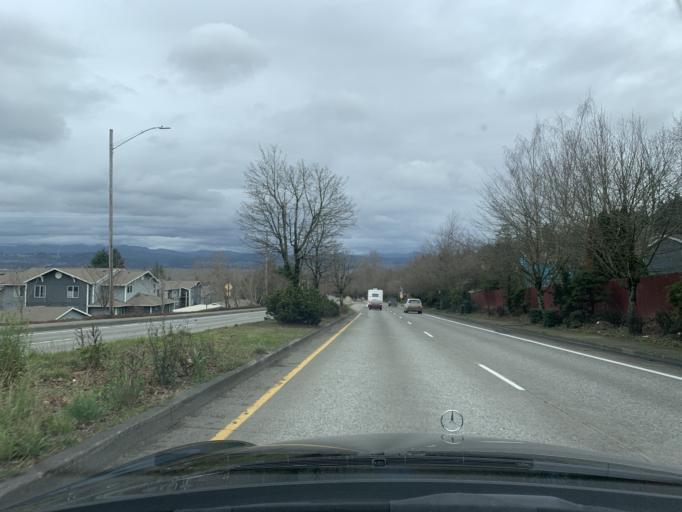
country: US
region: Oregon
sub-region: Multnomah County
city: Troutdale
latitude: 45.5352
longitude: -122.3981
